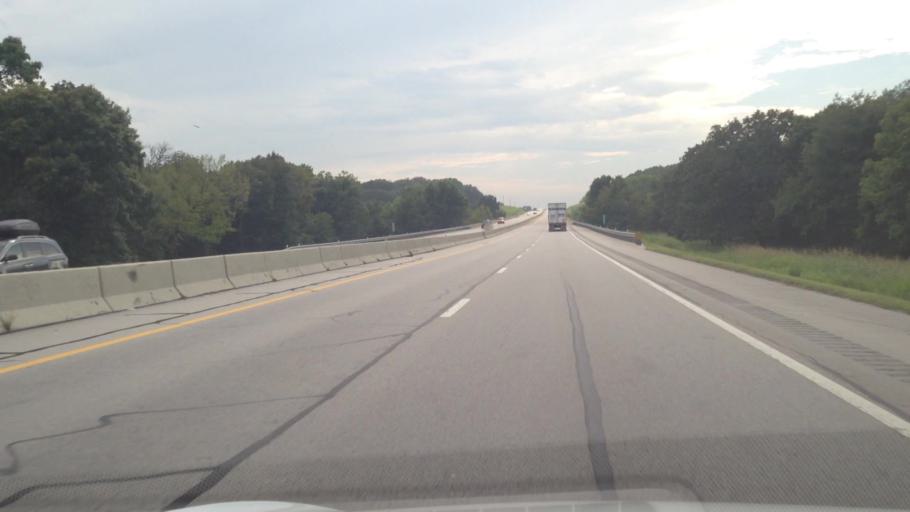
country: US
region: Kansas
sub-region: Cherokee County
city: Baxter Springs
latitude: 36.9270
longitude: -94.7378
